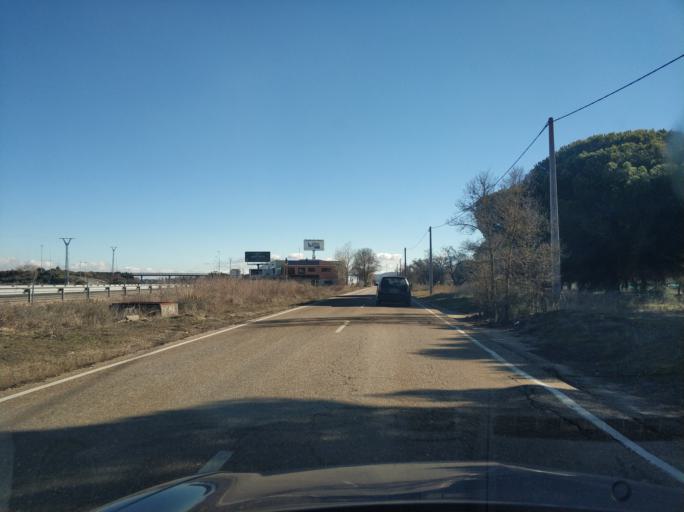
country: ES
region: Castille and Leon
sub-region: Provincia de Valladolid
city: Tudela de Duero
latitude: 41.5907
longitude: -4.6029
